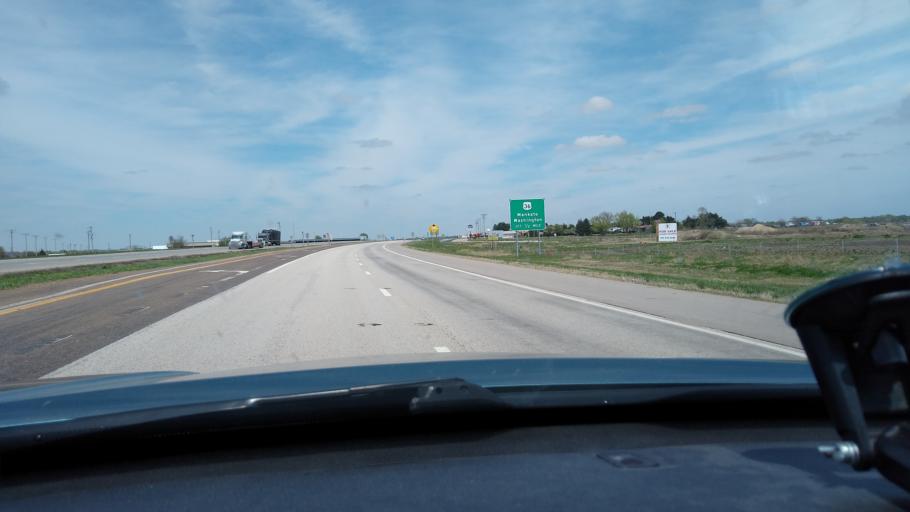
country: US
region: Kansas
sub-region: Republic County
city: Belleville
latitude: 39.8046
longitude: -97.6513
